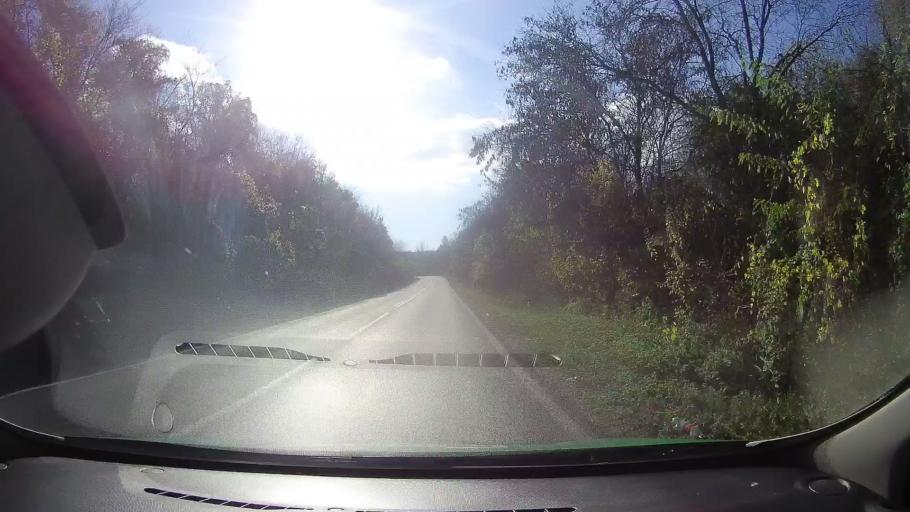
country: RO
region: Tulcea
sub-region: Oras Babadag
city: Babadag
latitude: 44.8719
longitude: 28.6886
